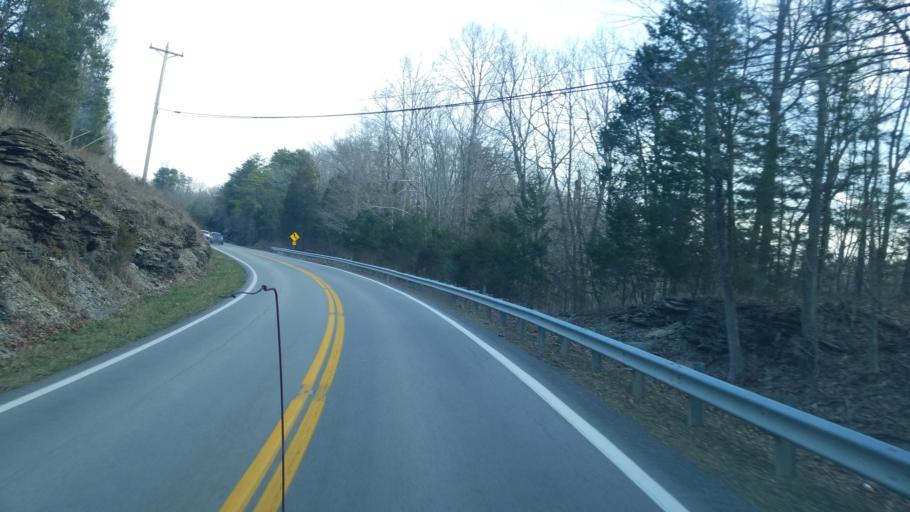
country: US
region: Kentucky
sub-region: Russell County
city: Jamestown
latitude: 36.8708
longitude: -85.1120
